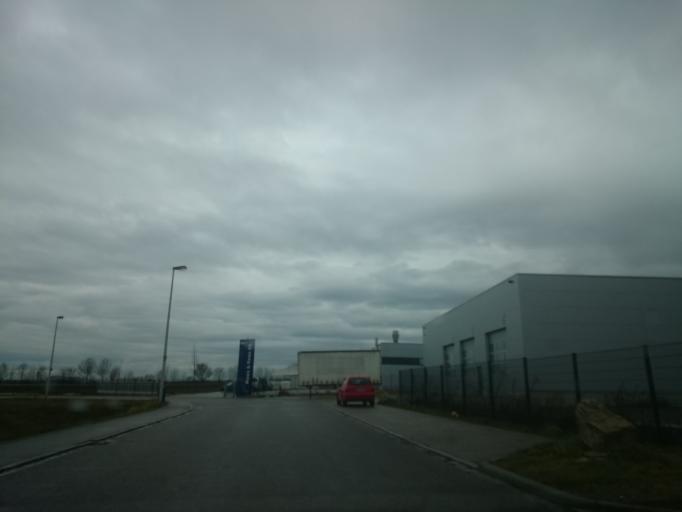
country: DE
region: Bavaria
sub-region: Regierungsbezirk Mittelfranken
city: Hilpoltstein
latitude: 49.1604
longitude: 11.2574
